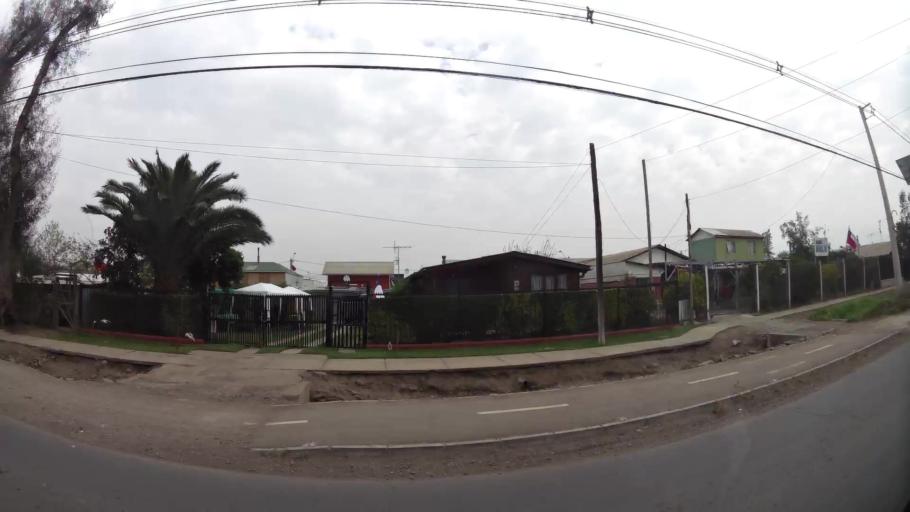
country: CL
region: Santiago Metropolitan
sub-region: Provincia de Chacabuco
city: Chicureo Abajo
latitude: -33.1995
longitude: -70.6788
